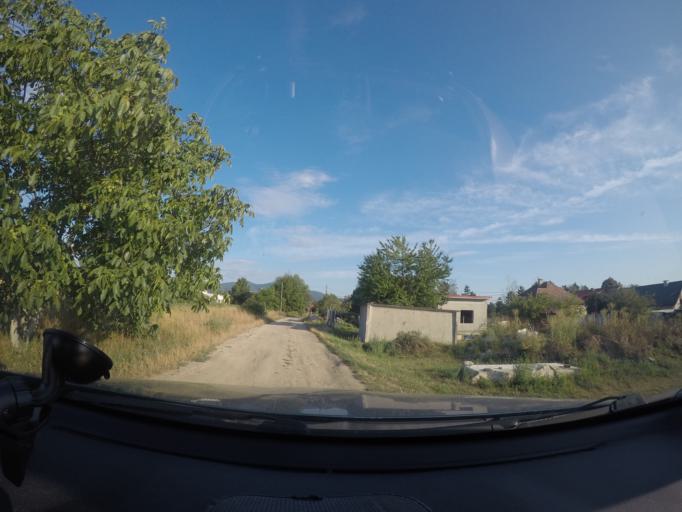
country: SK
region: Trenciansky
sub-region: Okres Trencin
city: Trencin
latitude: 48.8741
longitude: 18.0016
